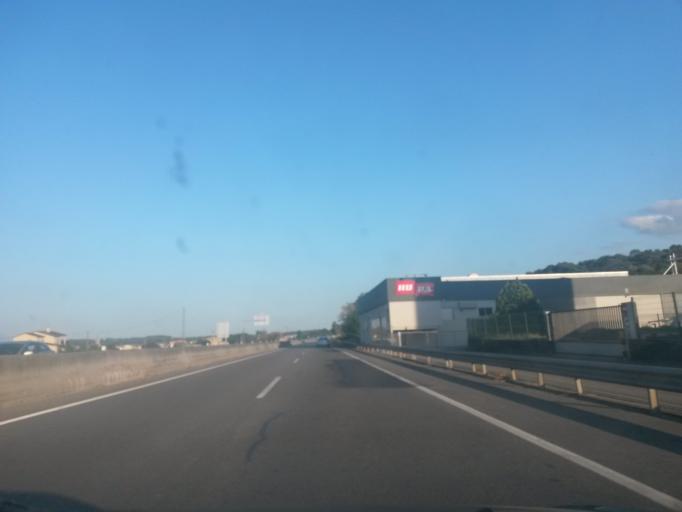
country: ES
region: Catalonia
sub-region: Provincia de Girona
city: Cornella del Terri
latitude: 42.0926
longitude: 2.8050
